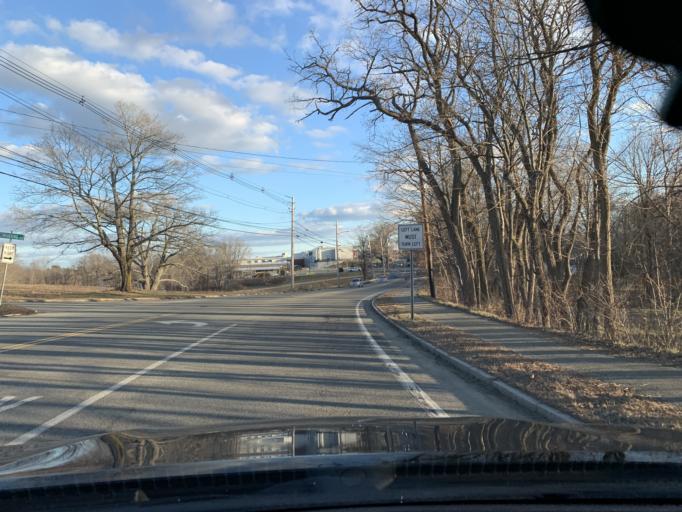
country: US
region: Massachusetts
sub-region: Essex County
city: Middleton
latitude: 42.5942
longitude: -70.9834
